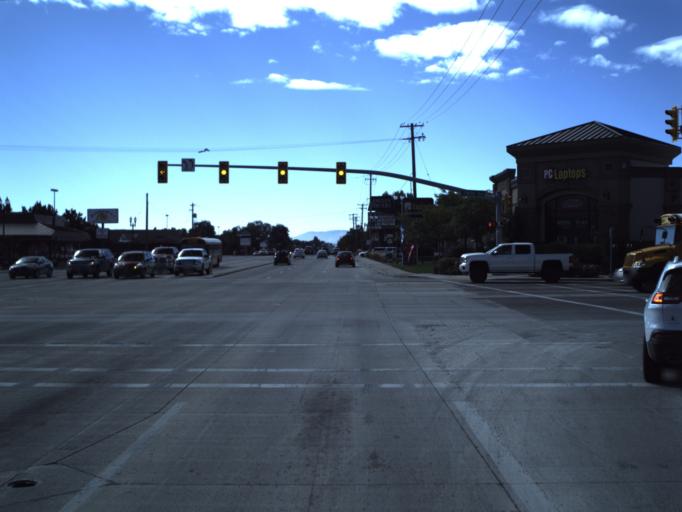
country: US
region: Utah
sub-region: Salt Lake County
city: West Jordan
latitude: 40.6098
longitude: -111.9389
